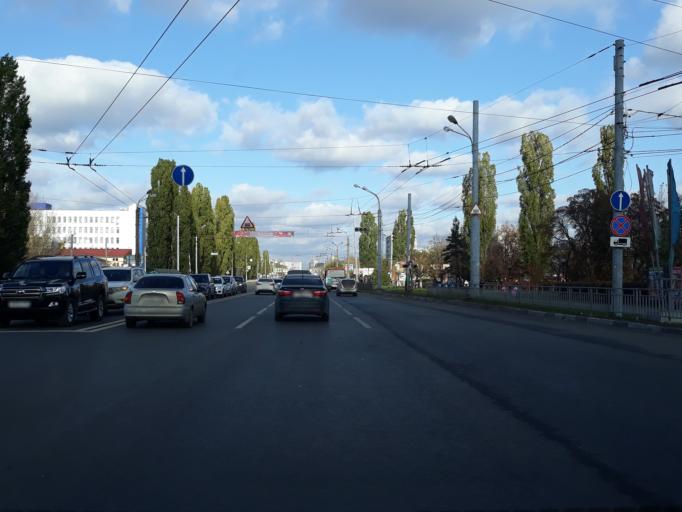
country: RU
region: Nizjnij Novgorod
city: Nizhniy Novgorod
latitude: 56.2842
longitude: 43.9273
